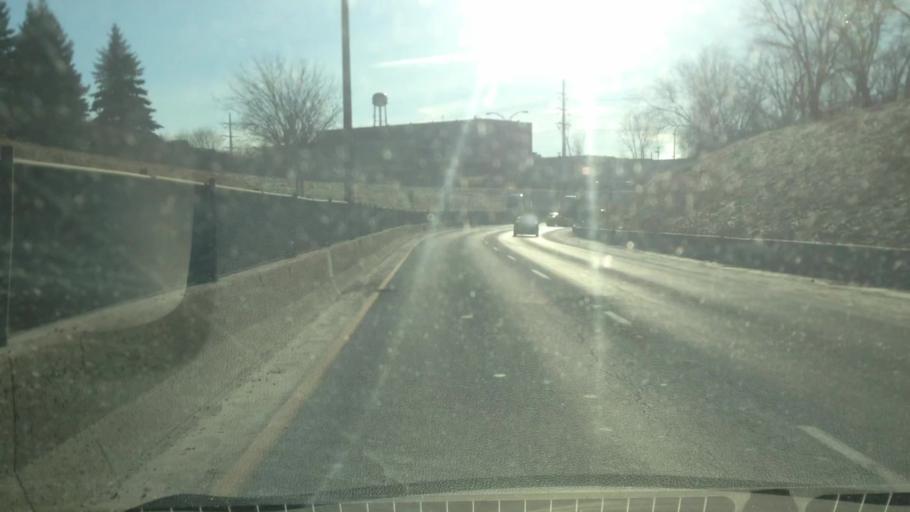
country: CA
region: Quebec
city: Montreal-Ouest
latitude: 45.4310
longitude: -73.6499
